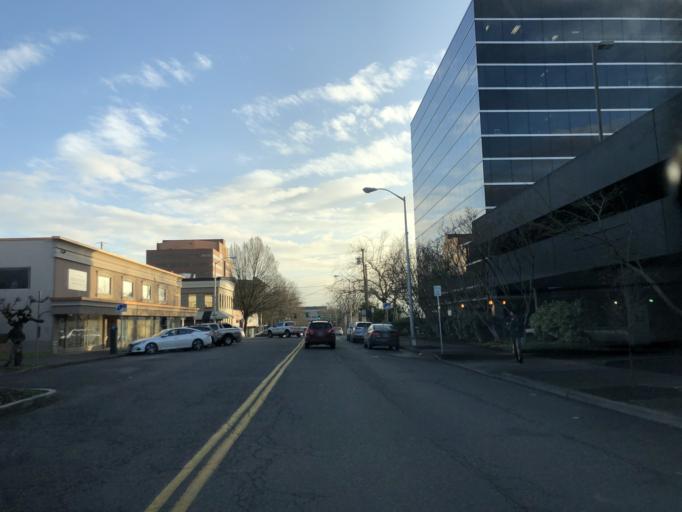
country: US
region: Washington
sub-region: Clark County
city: Vancouver
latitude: 45.6302
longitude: -122.6706
